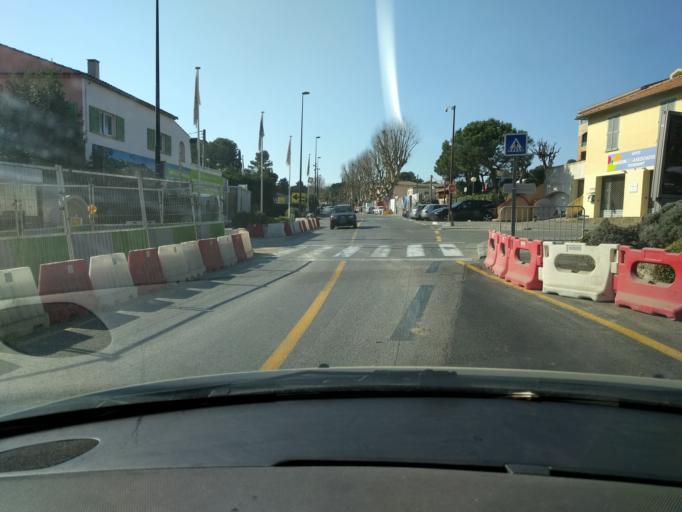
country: FR
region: Provence-Alpes-Cote d'Azur
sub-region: Departement des Alpes-Maritimes
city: Mougins
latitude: 43.6026
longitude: 6.9865
